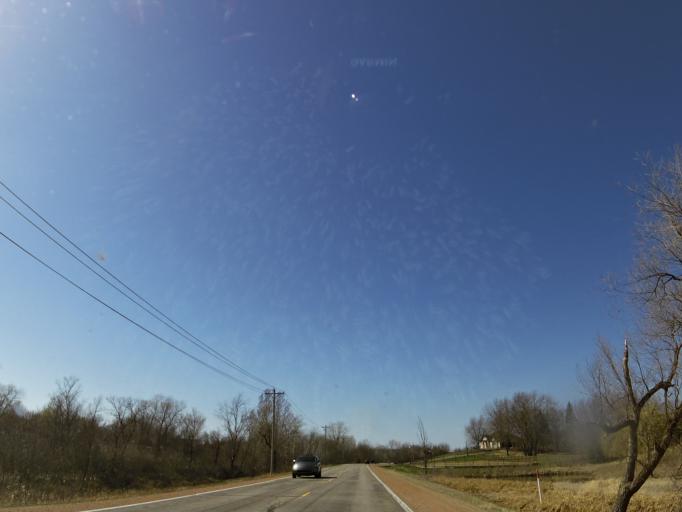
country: US
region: Minnesota
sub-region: Dakota County
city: Lakeville
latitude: 44.6569
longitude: -93.3296
